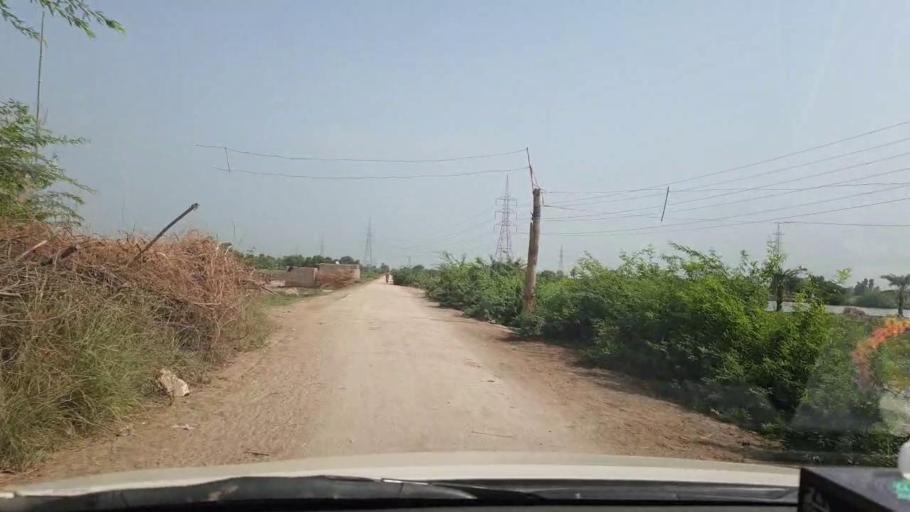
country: PK
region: Sindh
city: Shikarpur
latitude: 27.9740
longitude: 68.6649
